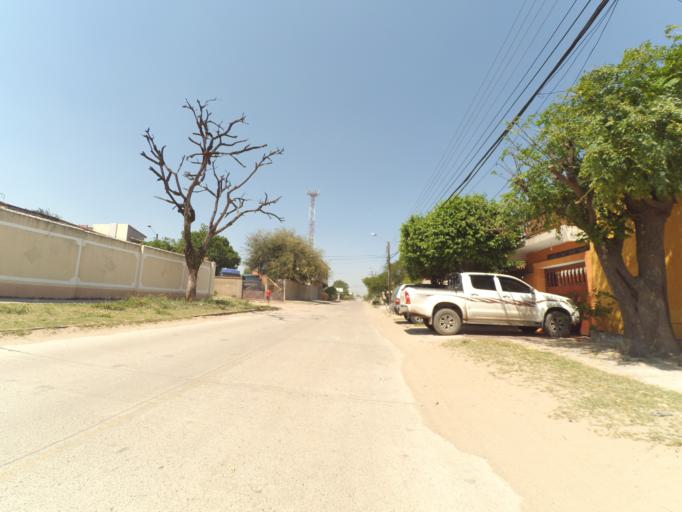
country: BO
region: Santa Cruz
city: Santa Cruz de la Sierra
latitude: -17.8101
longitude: -63.2126
